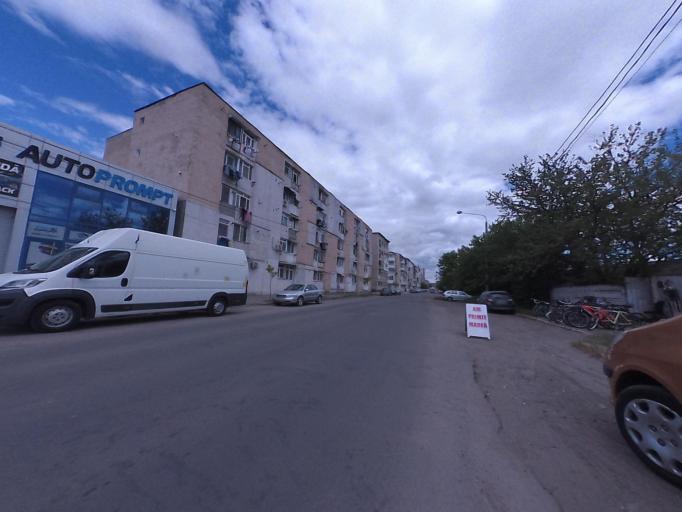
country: RO
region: Vaslui
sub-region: Municipiul Barlad
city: Barlad
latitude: 46.2142
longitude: 27.6689
